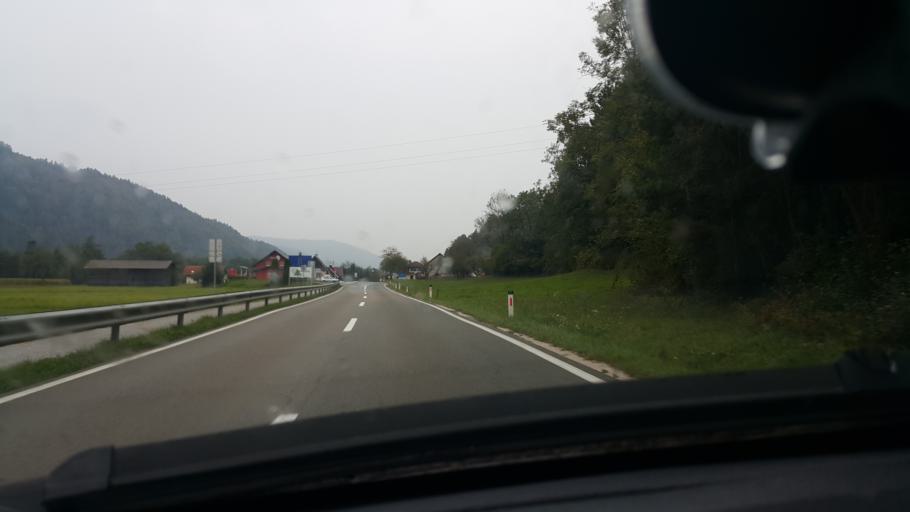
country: SI
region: Dravograd
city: Dravograd
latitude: 46.6023
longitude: 14.9889
